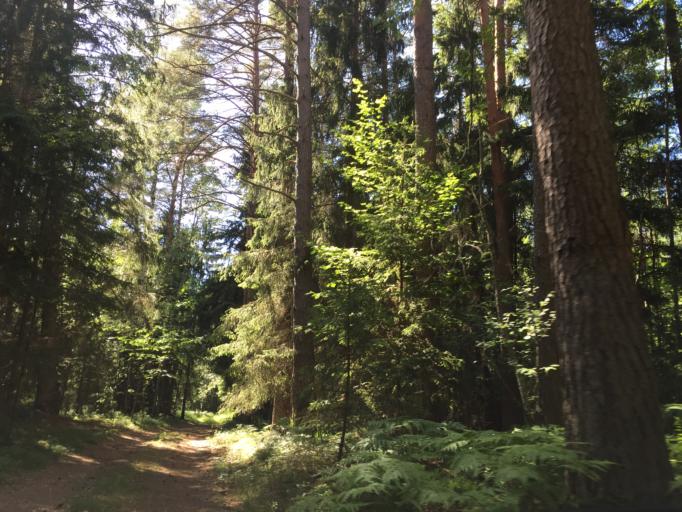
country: LV
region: Ventspils
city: Ventspils
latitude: 57.4720
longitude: 21.6542
